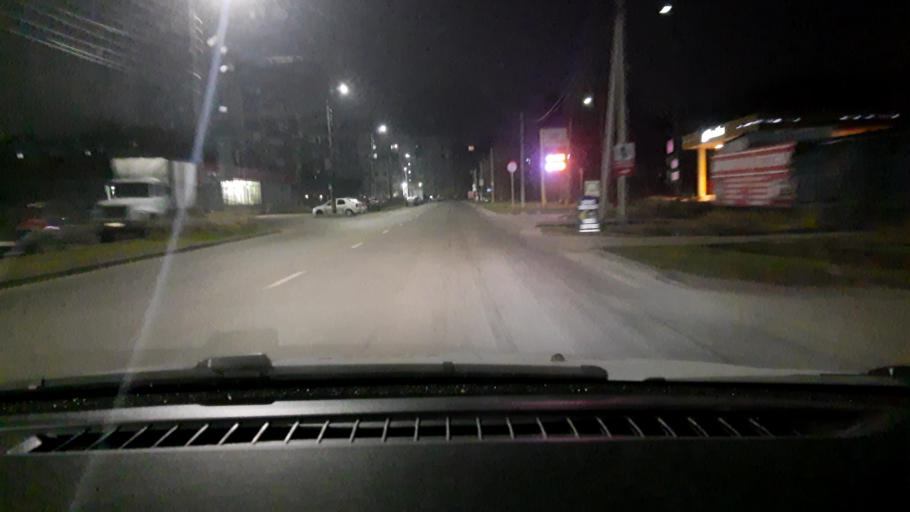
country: RU
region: Nizjnij Novgorod
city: Dzerzhinsk
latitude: 56.2565
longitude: 43.4571
